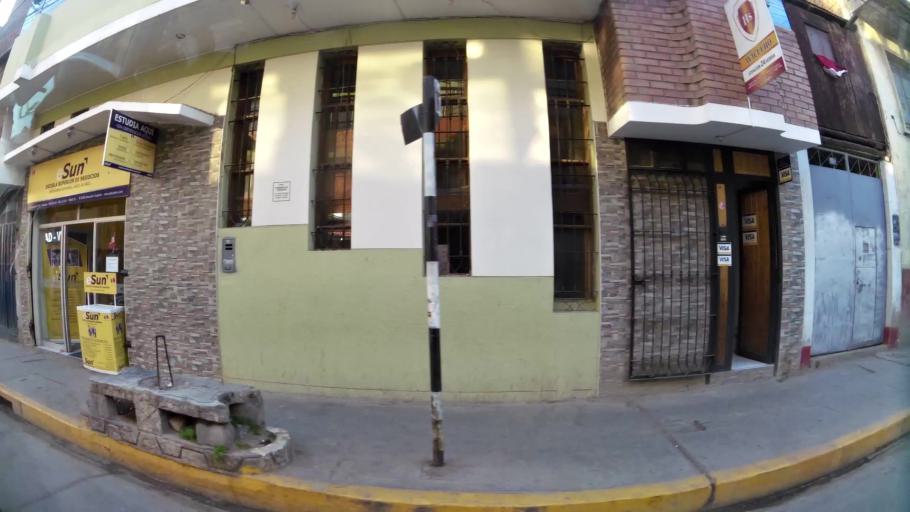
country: PE
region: Junin
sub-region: Provincia de Huancayo
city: Huancayo
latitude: -12.0649
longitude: -75.2091
